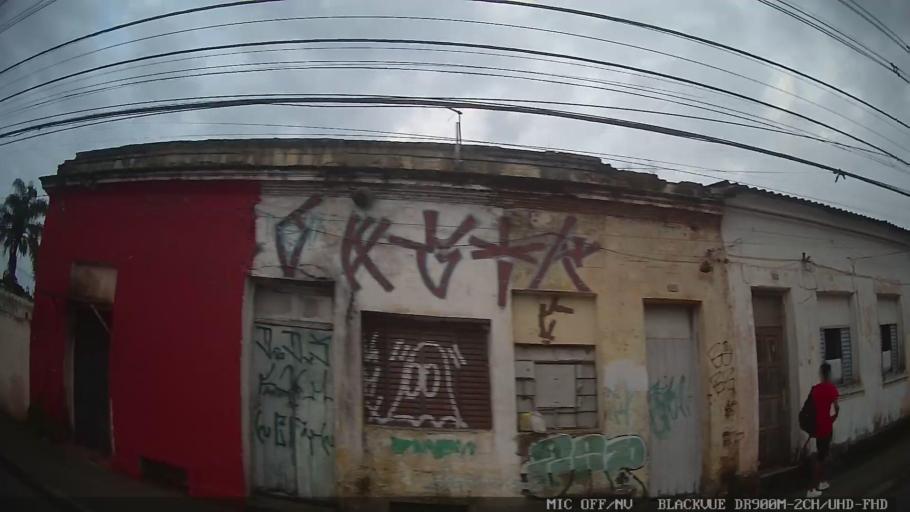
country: BR
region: Sao Paulo
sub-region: Suzano
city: Suzano
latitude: -23.5422
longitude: -46.2583
